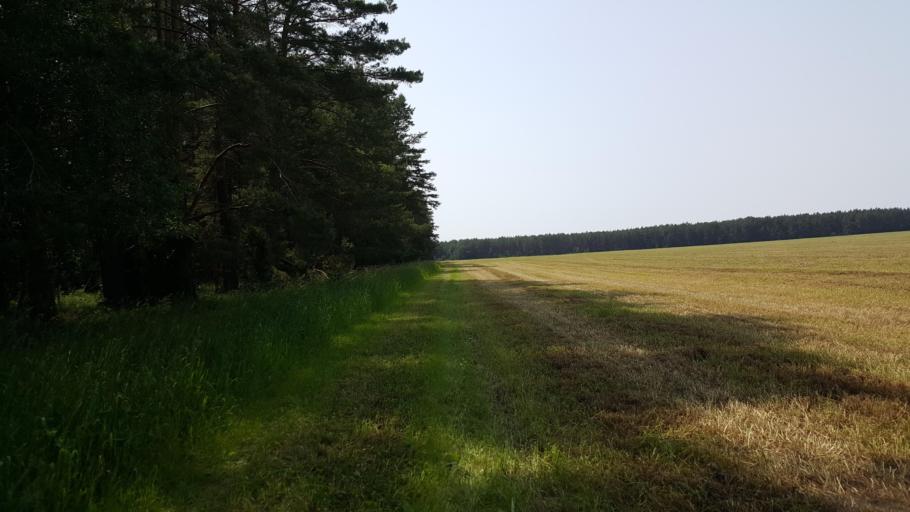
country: BY
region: Brest
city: Kamyanyuki
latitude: 52.5159
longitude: 23.8376
